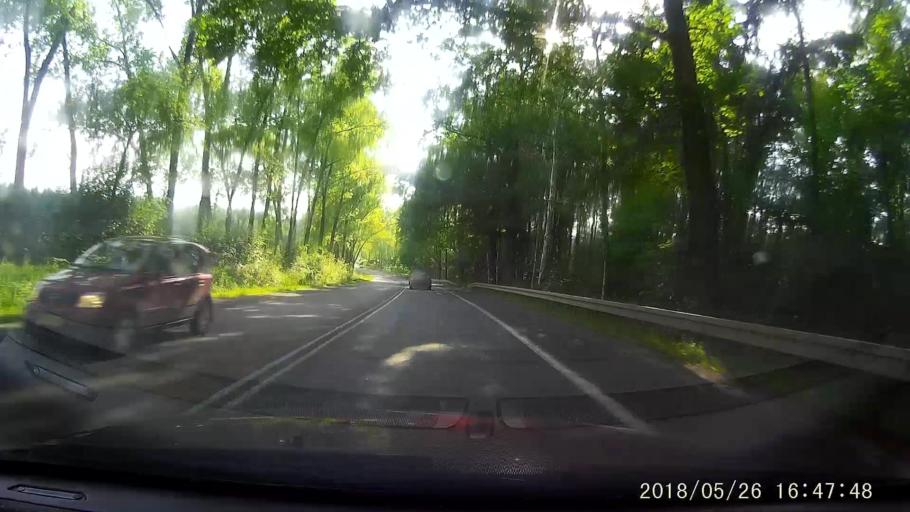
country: PL
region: Lower Silesian Voivodeship
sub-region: Powiat zgorzelecki
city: Sulikow
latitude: 51.0645
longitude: 14.9988
